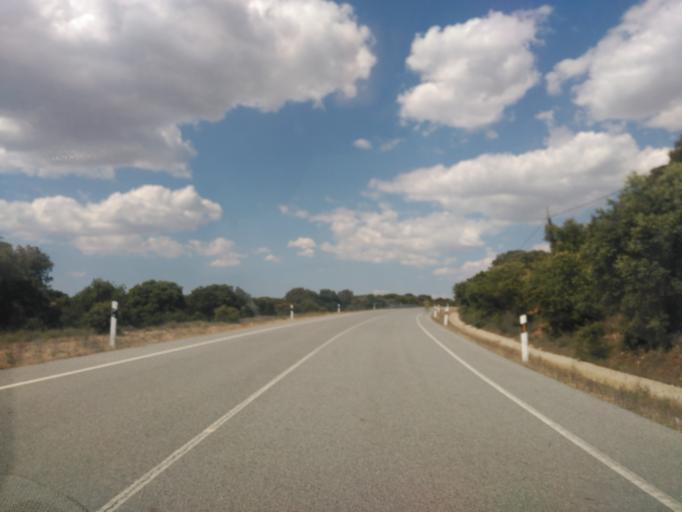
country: ES
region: Castille and Leon
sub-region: Provincia de Salamanca
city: Belena
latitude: 40.7315
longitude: -5.6322
